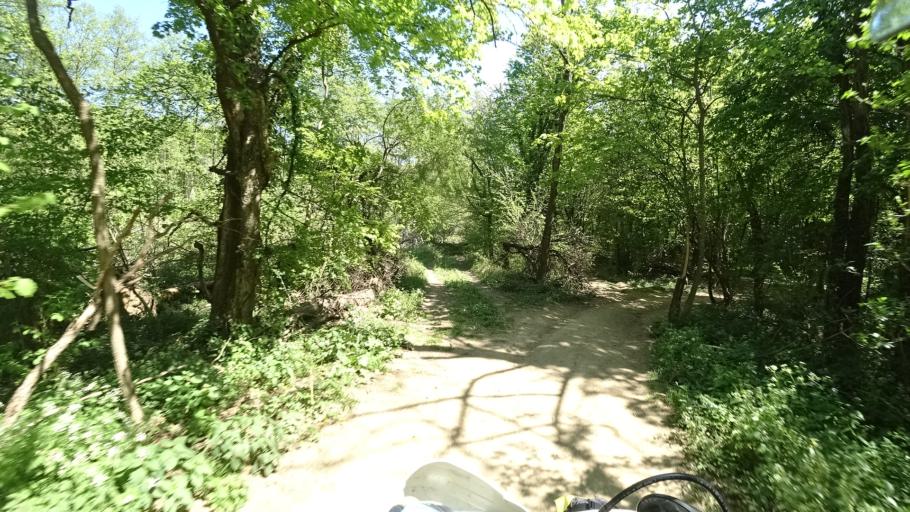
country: HR
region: Zagrebacka
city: Jablanovec
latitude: 45.8546
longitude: 15.8769
